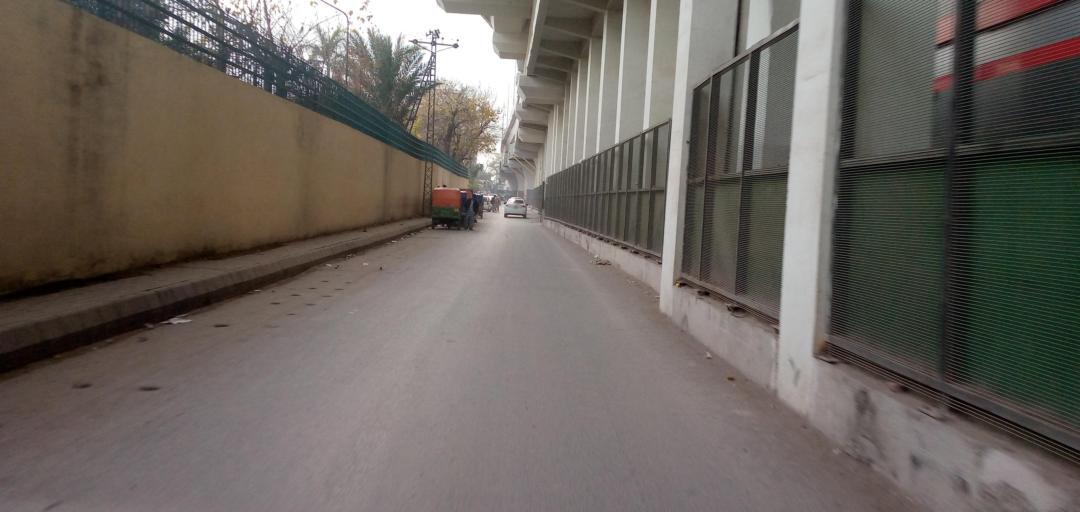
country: PK
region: Khyber Pakhtunkhwa
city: Peshawar
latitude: 34.0053
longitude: 71.5570
